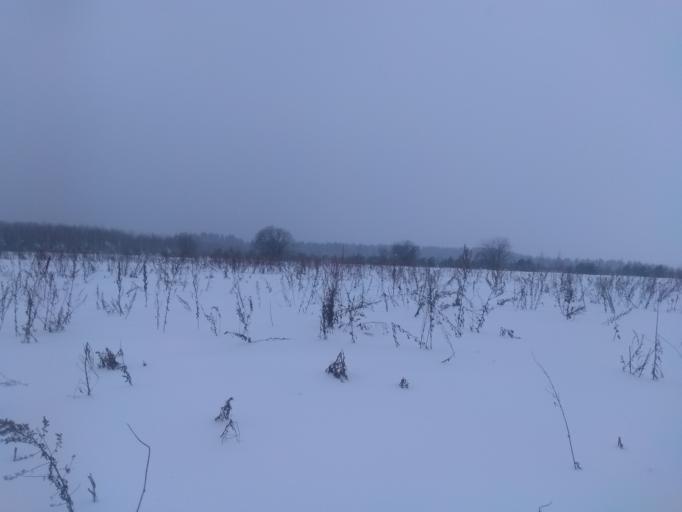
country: RU
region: Perm
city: Sylva
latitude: 57.8451
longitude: 56.7853
